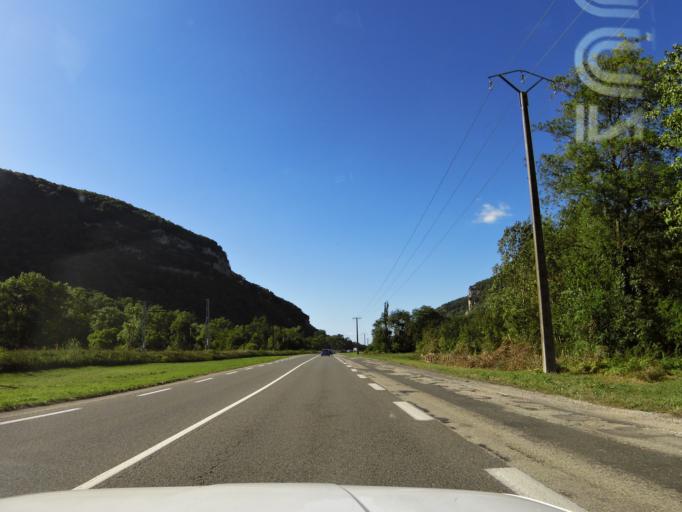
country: FR
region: Rhone-Alpes
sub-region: Departement de l'Ain
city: Vaux-en-Bugey
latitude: 45.9208
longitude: 5.3935
